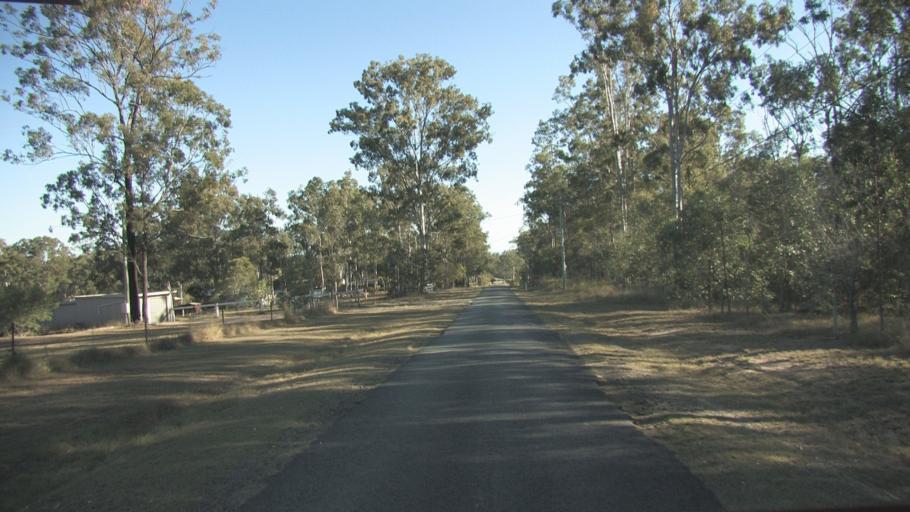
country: AU
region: Queensland
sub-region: Logan
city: North Maclean
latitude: -27.8110
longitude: 153.0491
